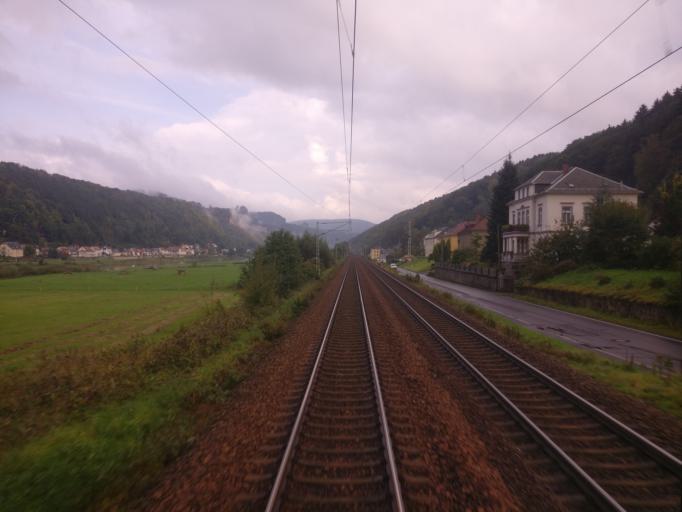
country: DE
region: Saxony
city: Bad Schandau
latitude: 50.9126
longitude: 14.1628
